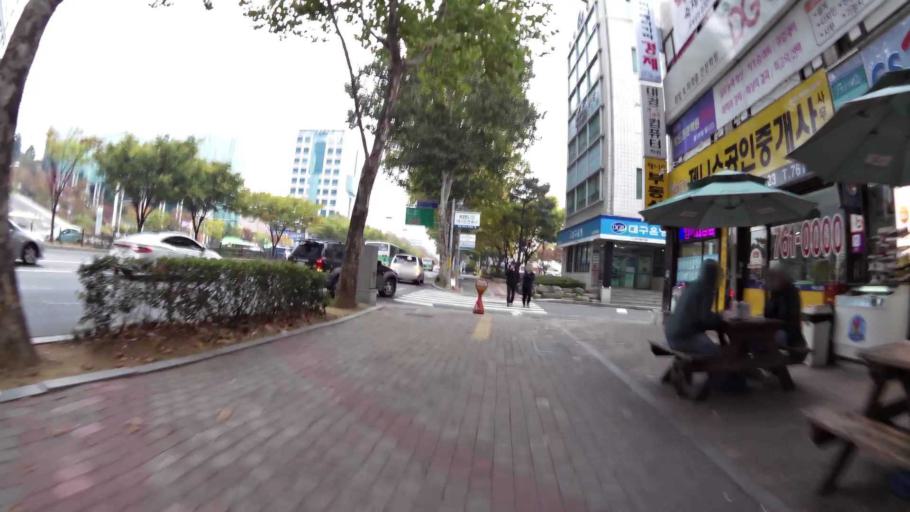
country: KR
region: Daegu
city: Daegu
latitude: 35.8587
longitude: 128.6297
